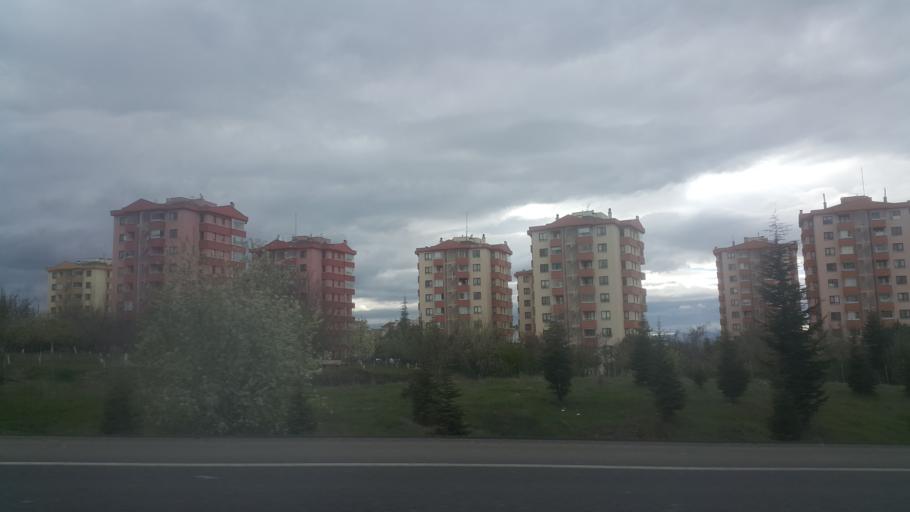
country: TR
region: Ankara
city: Etimesgut
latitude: 39.9318
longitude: 32.6243
